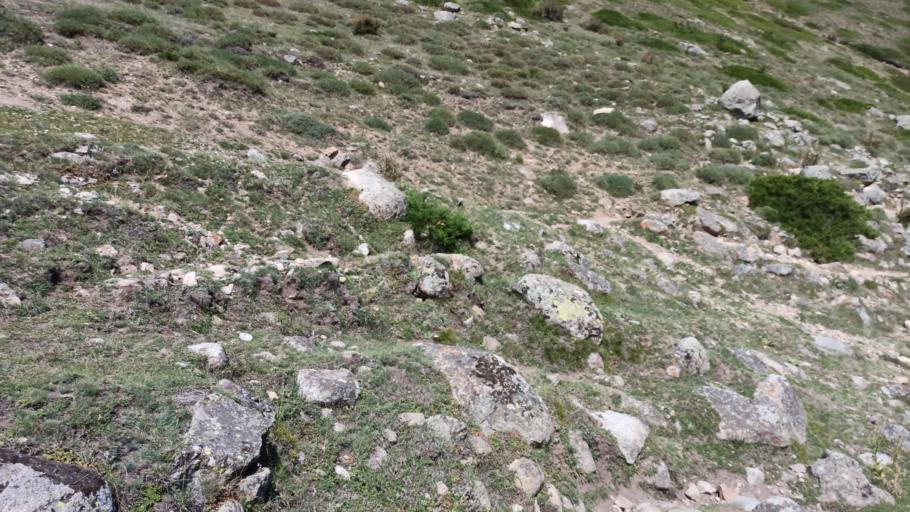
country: RU
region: Kabardino-Balkariya
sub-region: El'brusskiy Rayon
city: El'brus
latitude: 43.2624
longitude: 42.6412
